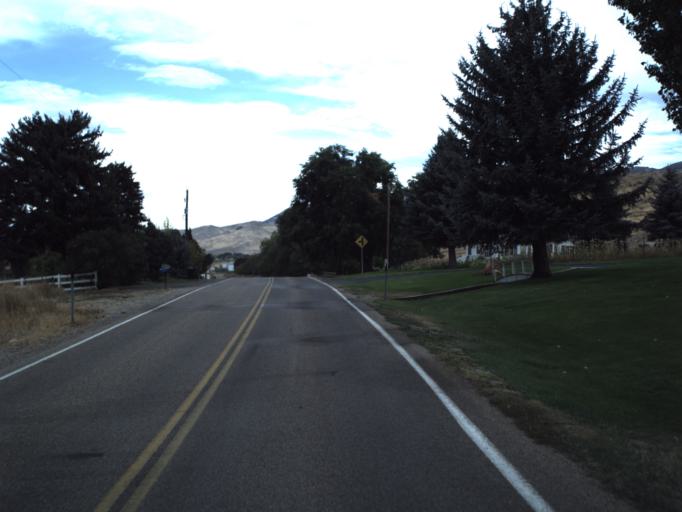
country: US
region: Utah
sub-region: Morgan County
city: Morgan
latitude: 41.0065
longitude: -111.6758
